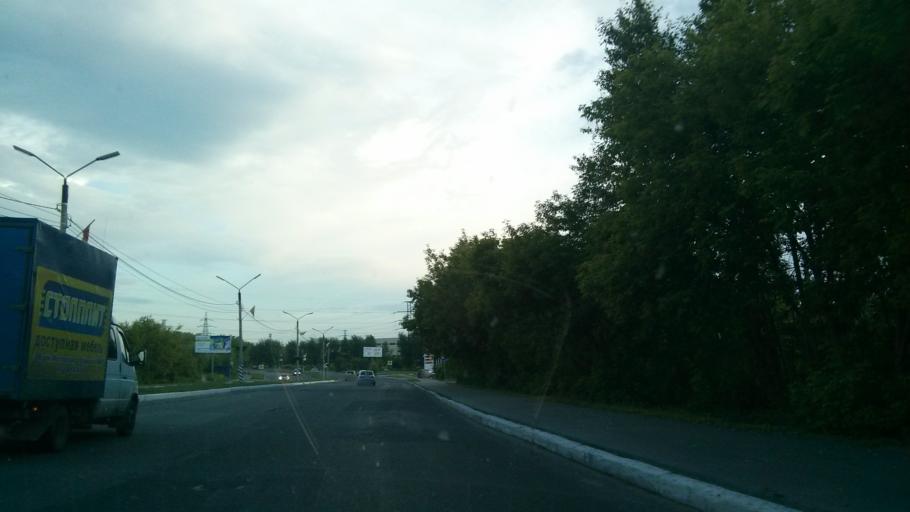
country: RU
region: Vladimir
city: Murom
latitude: 55.5626
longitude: 42.0602
